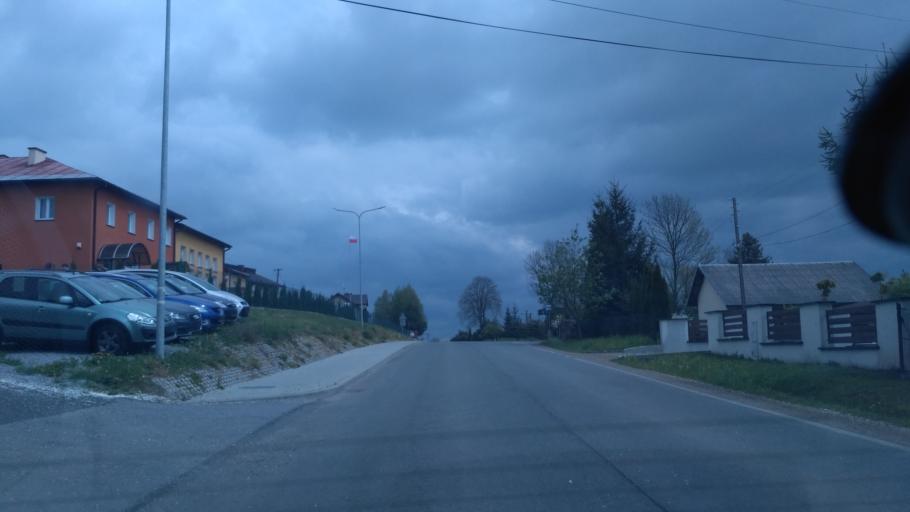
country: PL
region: Subcarpathian Voivodeship
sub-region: Powiat brzozowski
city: Jasionow
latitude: 49.6434
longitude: 21.9617
